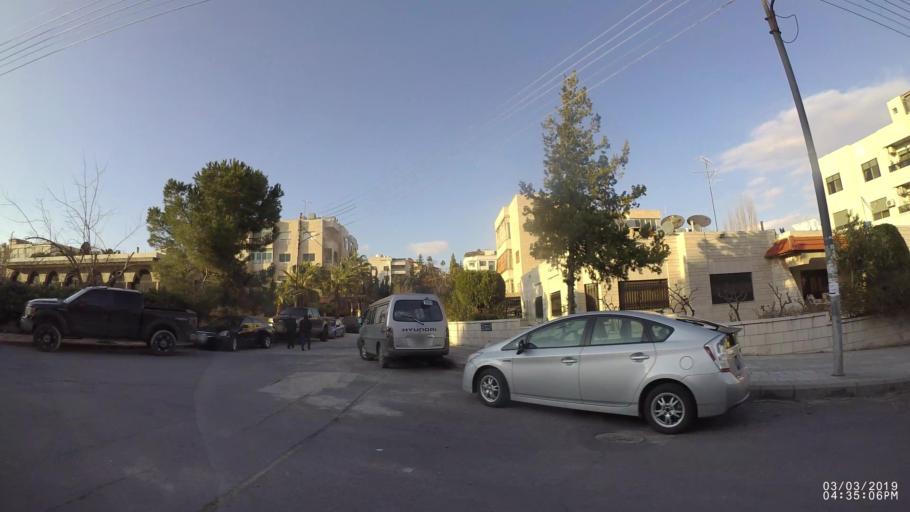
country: JO
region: Amman
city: Al Jubayhah
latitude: 31.9740
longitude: 35.8779
